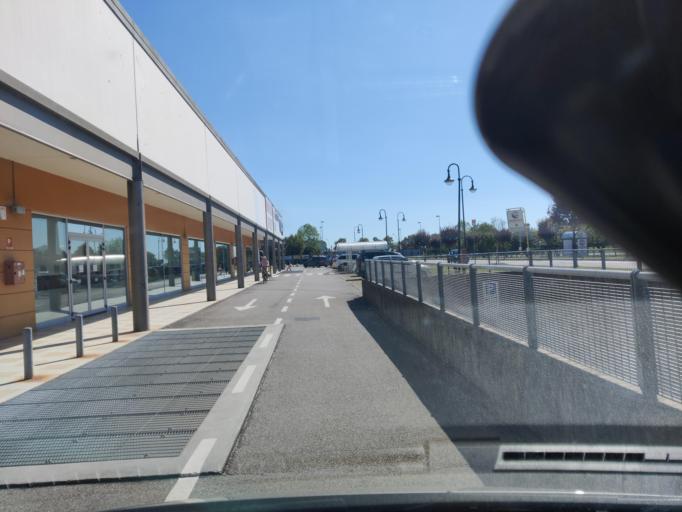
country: IT
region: Veneto
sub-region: Provincia di Treviso
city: Vittorio Veneto
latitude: 45.9824
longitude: 12.3142
